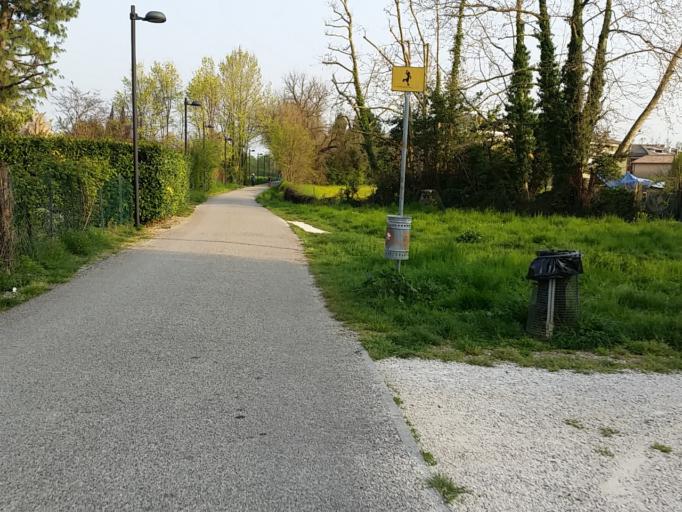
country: IT
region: Veneto
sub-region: Provincia di Padova
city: Padova
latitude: 45.3961
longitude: 11.8941
